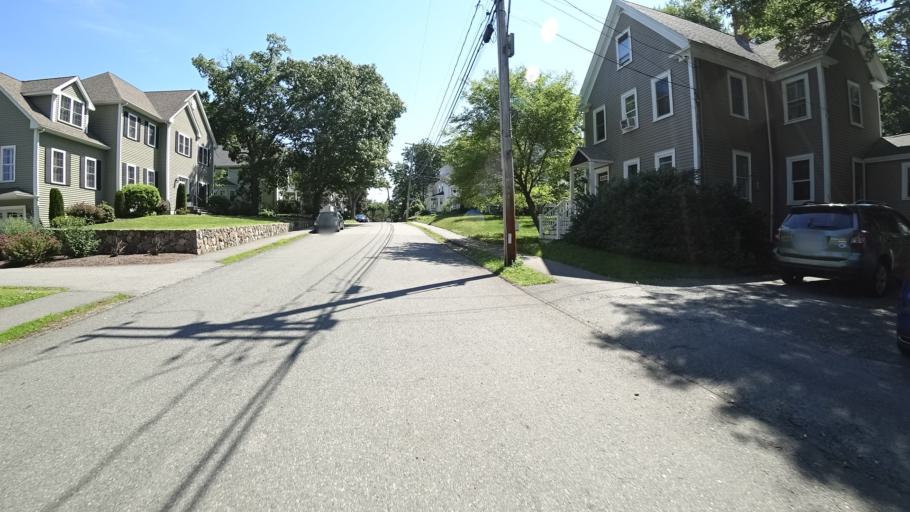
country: US
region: Massachusetts
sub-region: Norfolk County
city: Dedham
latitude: 42.2451
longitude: -71.1678
